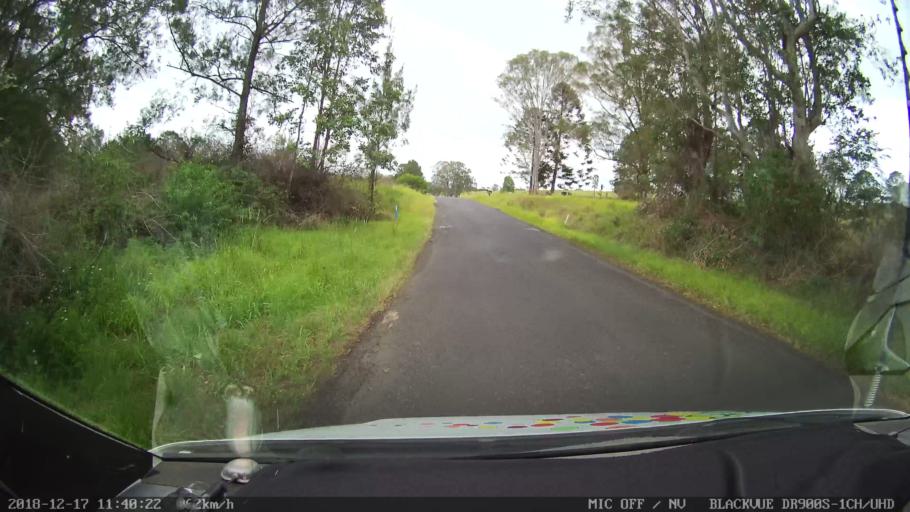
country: AU
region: New South Wales
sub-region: Kyogle
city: Kyogle
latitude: -28.6830
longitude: 152.5933
